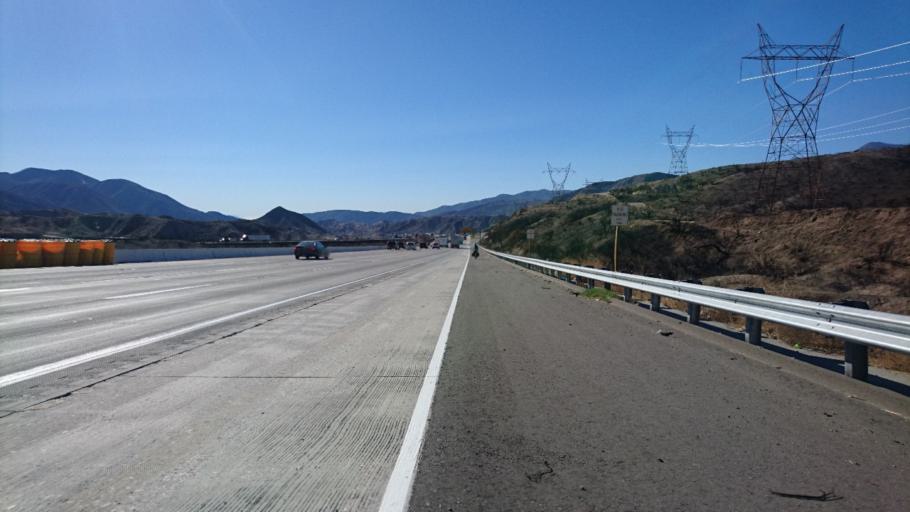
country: US
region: California
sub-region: San Bernardino County
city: Oak Hills
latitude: 34.3387
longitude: -117.4827
